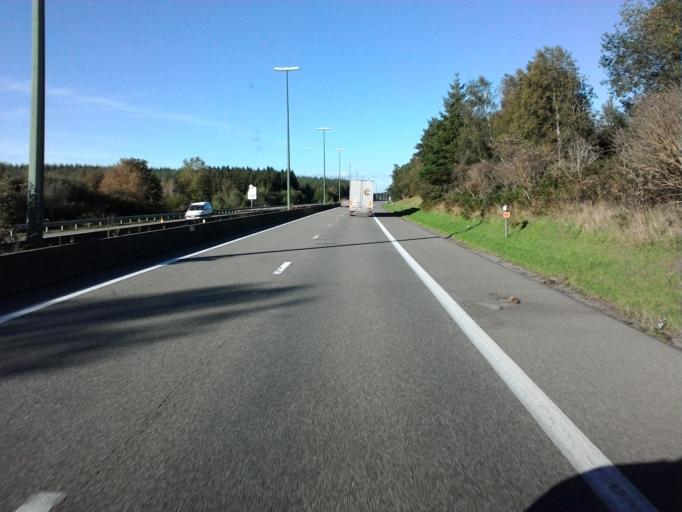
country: BE
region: Wallonia
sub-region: Province du Luxembourg
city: Bastogne
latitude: 50.0362
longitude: 5.7037
